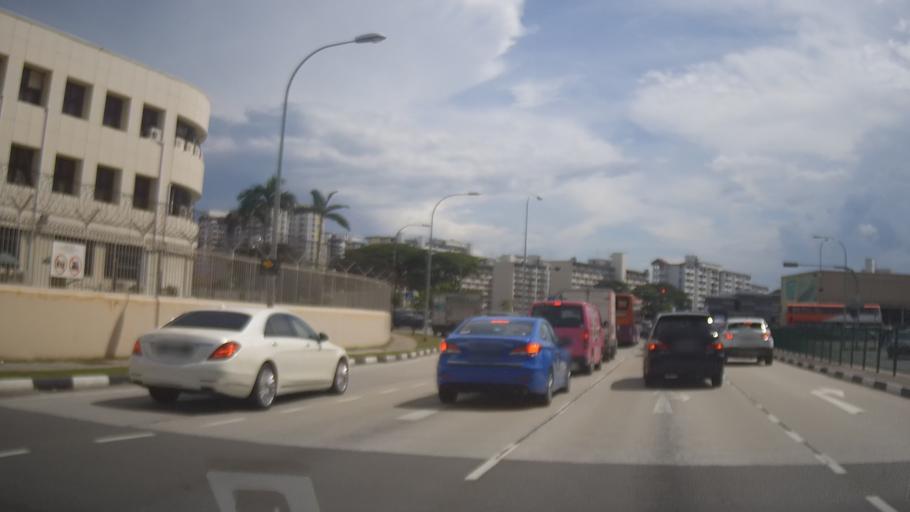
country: SG
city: Singapore
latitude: 1.3268
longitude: 103.8913
